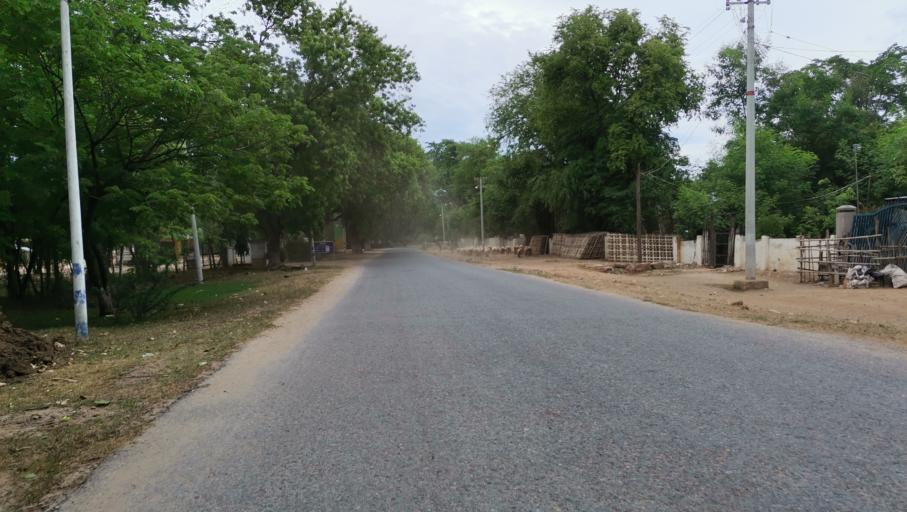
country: MM
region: Mandalay
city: Myingyan
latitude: 21.8420
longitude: 95.4270
